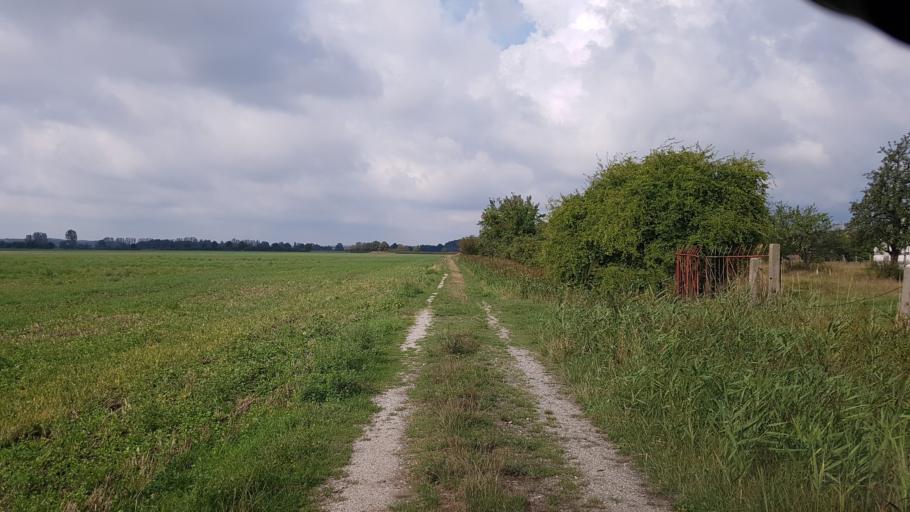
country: DE
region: Brandenburg
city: Ruckersdorf
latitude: 51.5742
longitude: 13.5610
